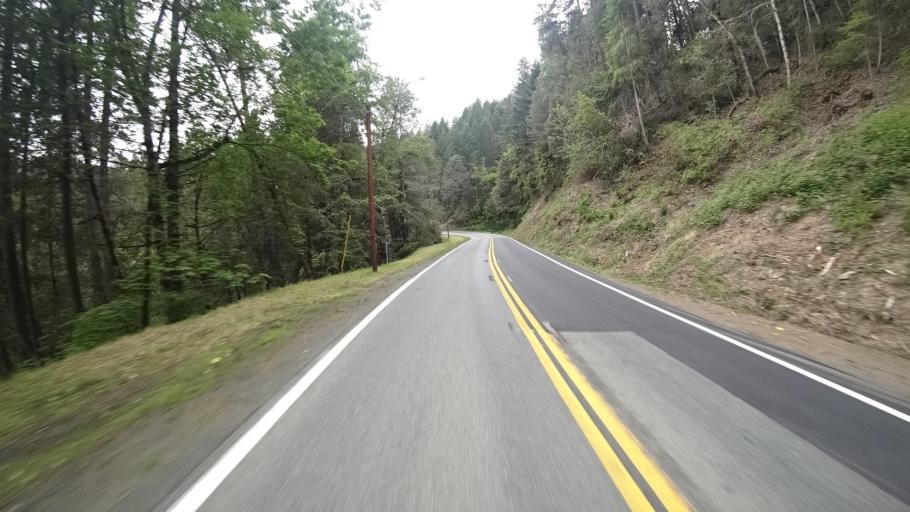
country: US
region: California
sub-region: Humboldt County
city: Willow Creek
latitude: 41.0081
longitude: -123.6475
